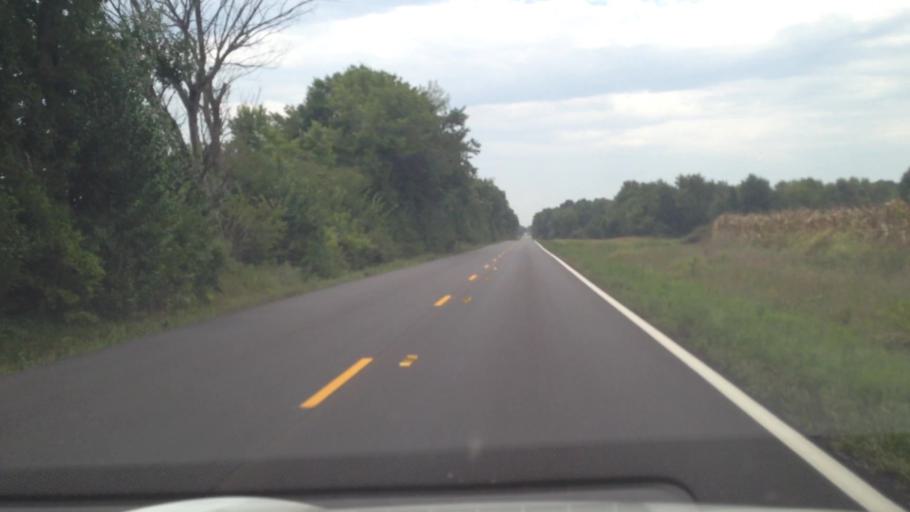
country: US
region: Kansas
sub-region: Crawford County
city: Girard
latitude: 37.5265
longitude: -94.9606
